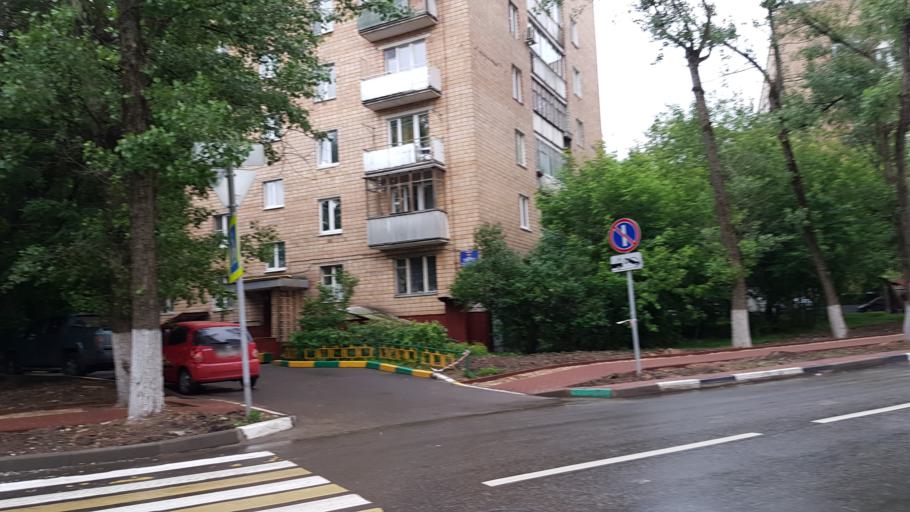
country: RU
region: Moscow
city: Khimki
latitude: 55.8921
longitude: 37.4524
